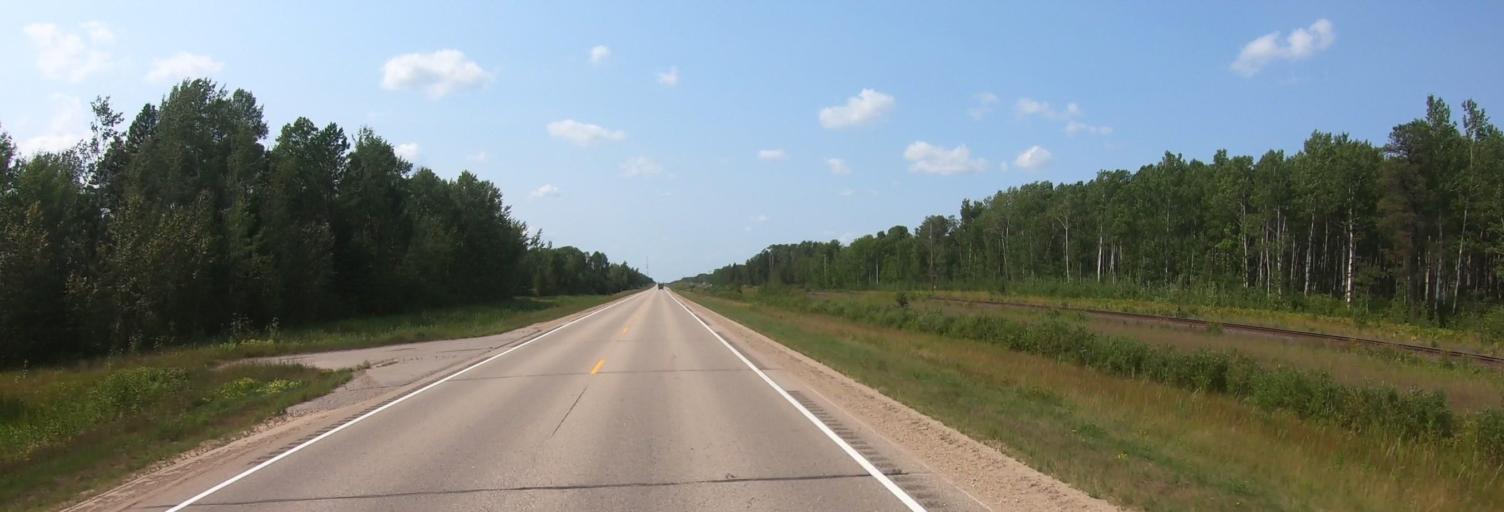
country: US
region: Minnesota
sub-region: Roseau County
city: Warroad
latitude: 48.7813
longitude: -95.0156
